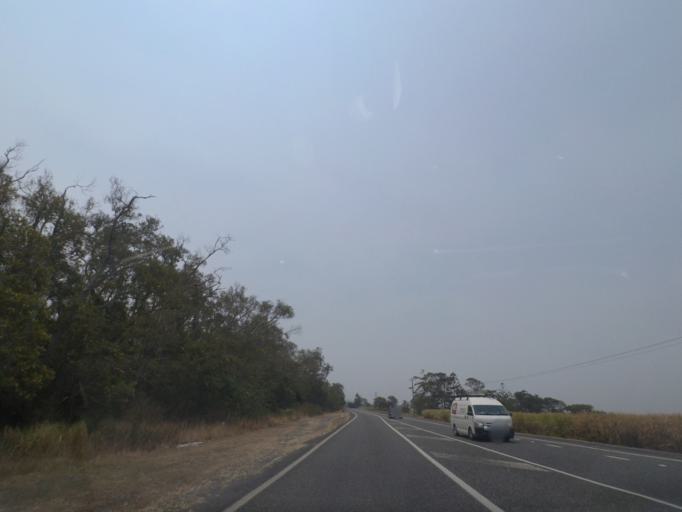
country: AU
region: New South Wales
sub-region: Ballina
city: Ballina
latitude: -28.9678
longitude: 153.4619
